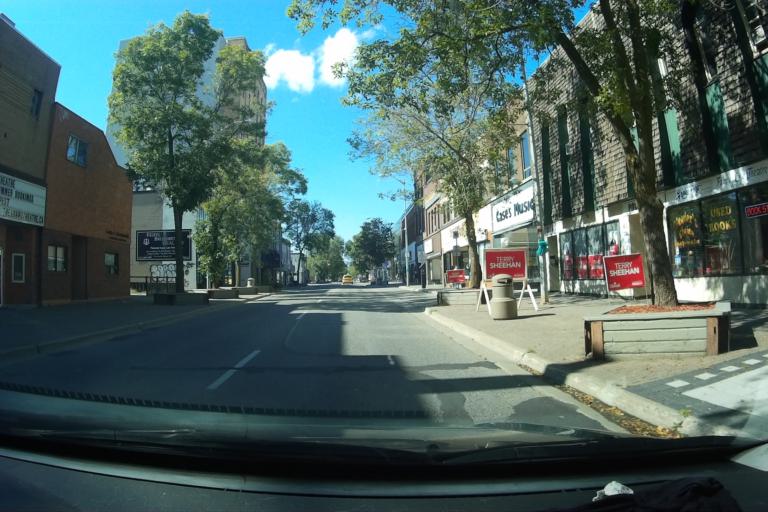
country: CA
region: Ontario
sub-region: Algoma
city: Sault Ste. Marie
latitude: 46.5084
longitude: -84.3288
